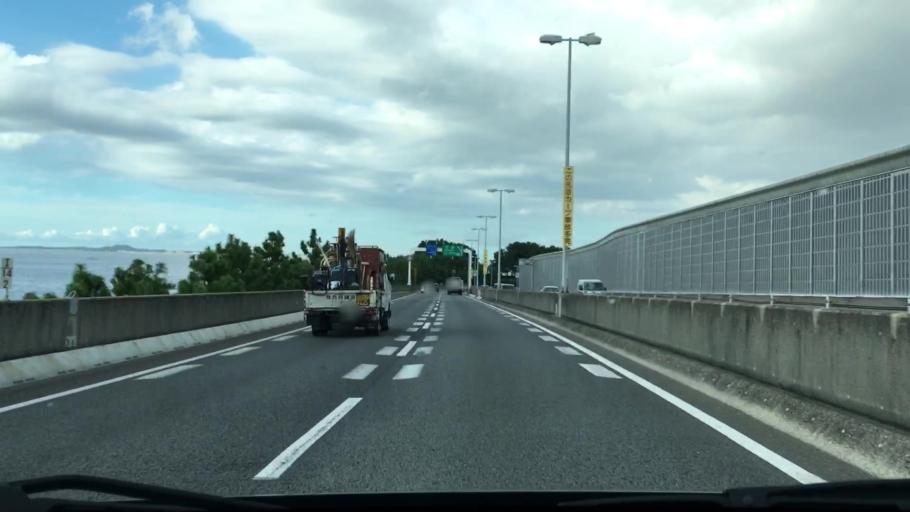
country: JP
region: Fukuoka
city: Fukuoka-shi
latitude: 33.5907
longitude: 130.3454
